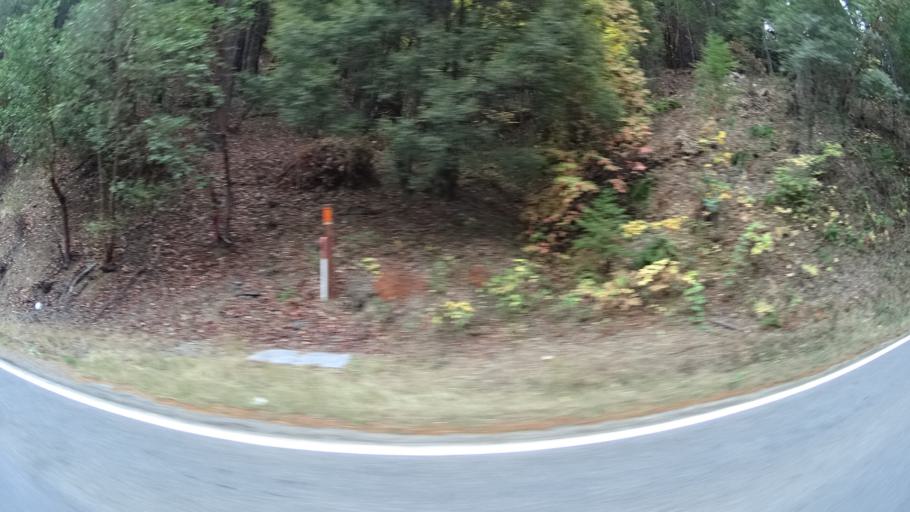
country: US
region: California
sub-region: Siskiyou County
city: Happy Camp
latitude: 41.8249
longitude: -123.3813
